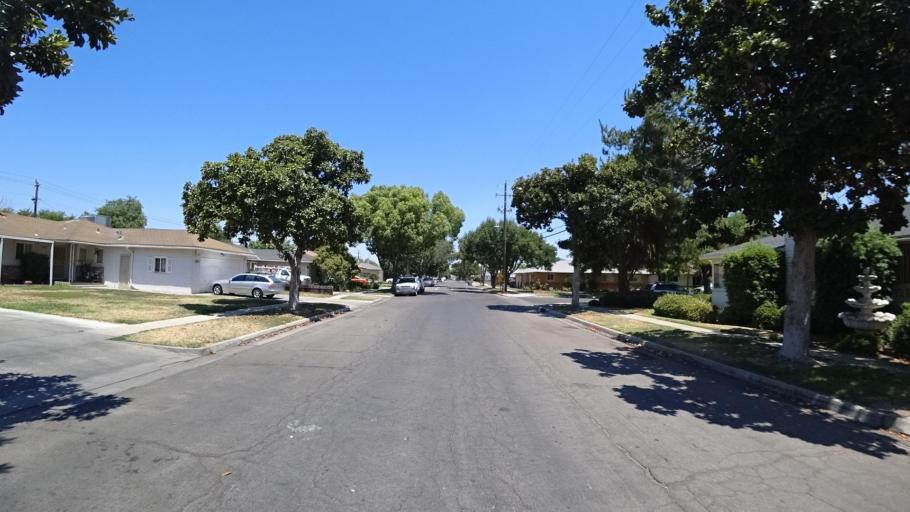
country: US
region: California
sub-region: Fresno County
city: Fresno
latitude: 36.7978
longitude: -119.7673
